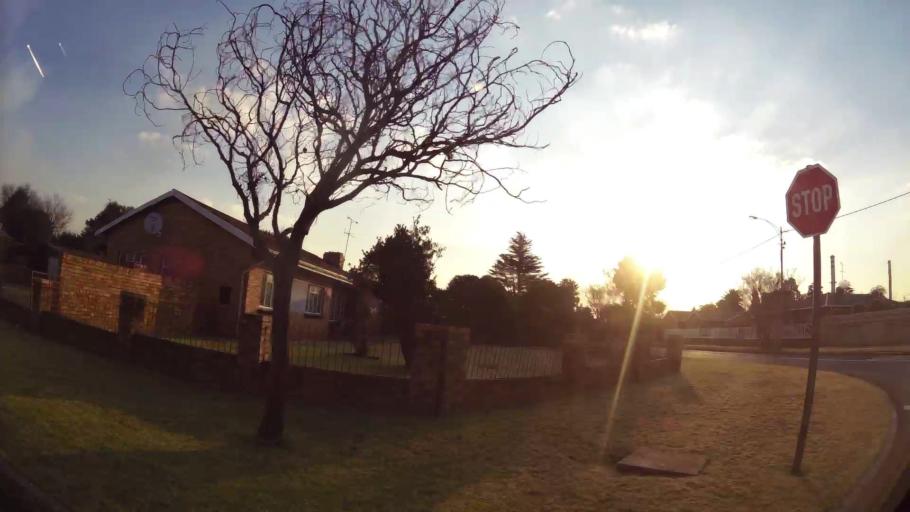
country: ZA
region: Gauteng
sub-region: Ekurhuleni Metropolitan Municipality
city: Springs
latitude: -26.2652
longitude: 28.4145
